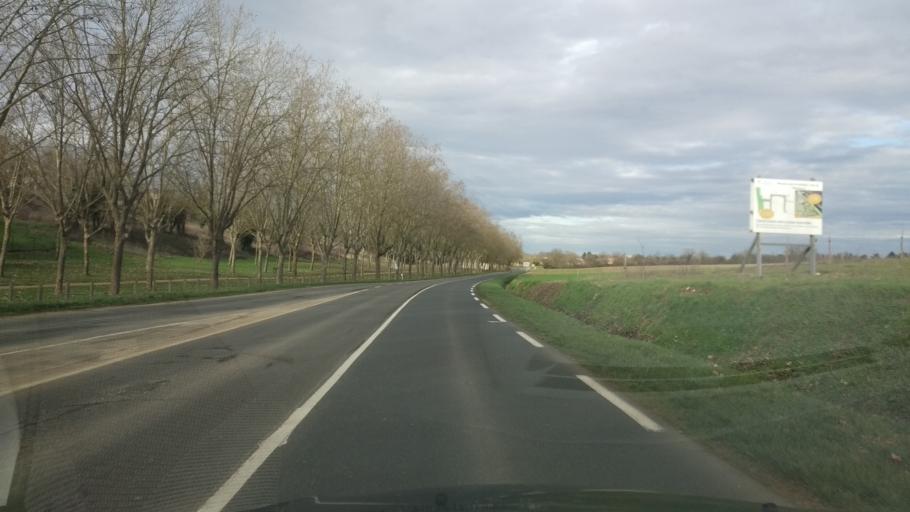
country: FR
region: Poitou-Charentes
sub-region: Departement de la Vienne
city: Saint-Georges-les-Baillargeaux
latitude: 46.6740
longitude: 0.4057
